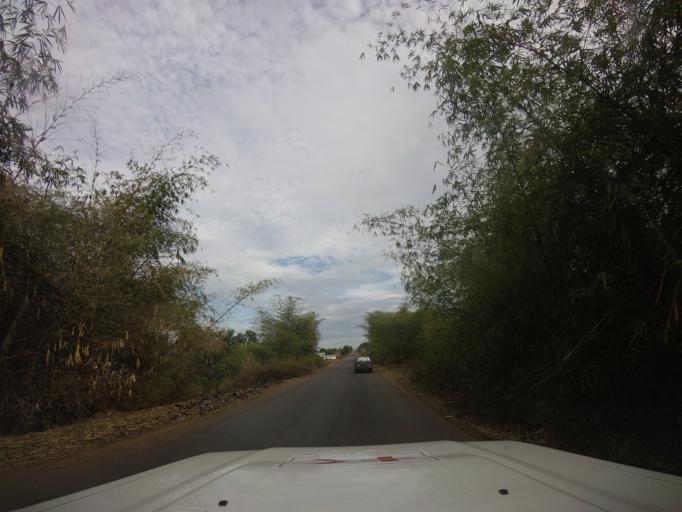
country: LR
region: Bomi
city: Tubmanburg
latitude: 6.7192
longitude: -10.9775
